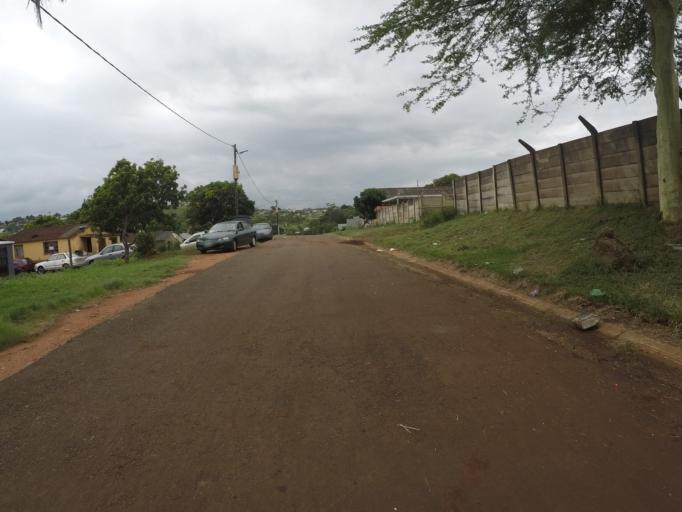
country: ZA
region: KwaZulu-Natal
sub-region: uThungulu District Municipality
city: Empangeni
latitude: -28.7755
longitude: 31.8614
